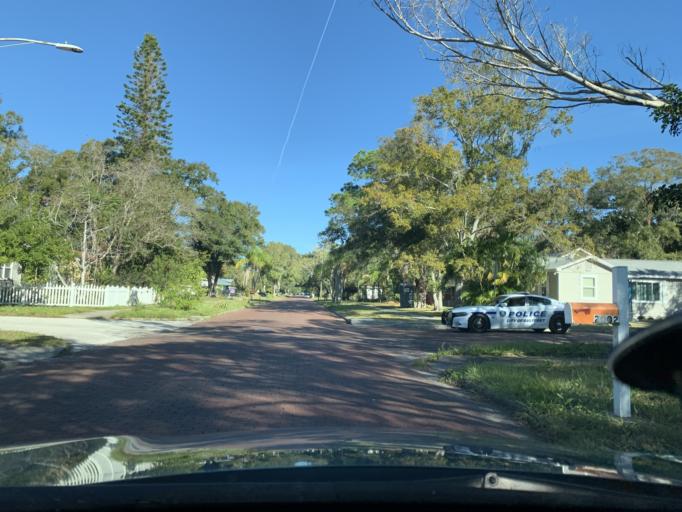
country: US
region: Florida
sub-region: Pinellas County
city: Gulfport
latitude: 27.7499
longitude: -82.7051
